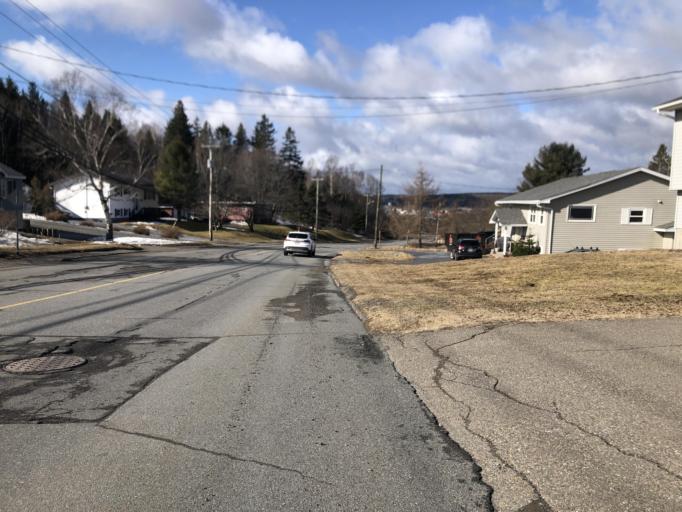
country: CA
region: New Brunswick
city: Saint John
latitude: 45.3193
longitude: -66.0058
